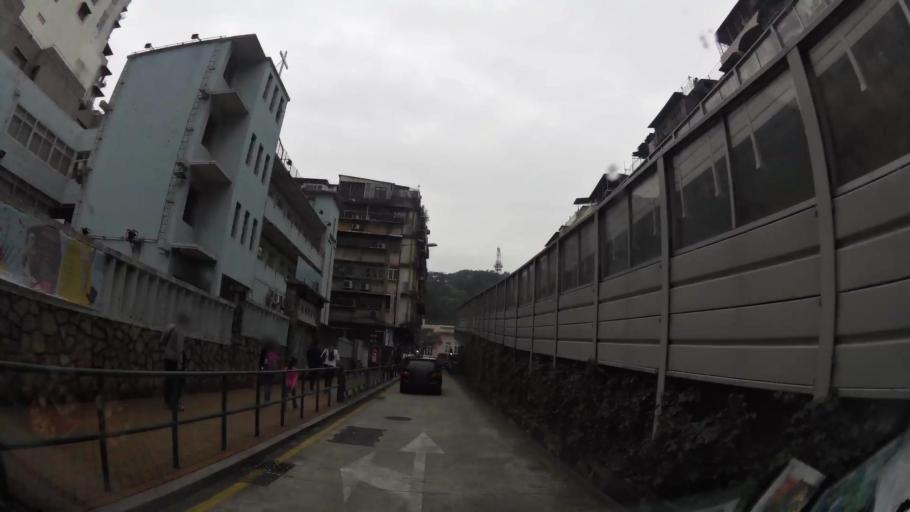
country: MO
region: Macau
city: Macau
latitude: 22.2009
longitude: 113.5495
